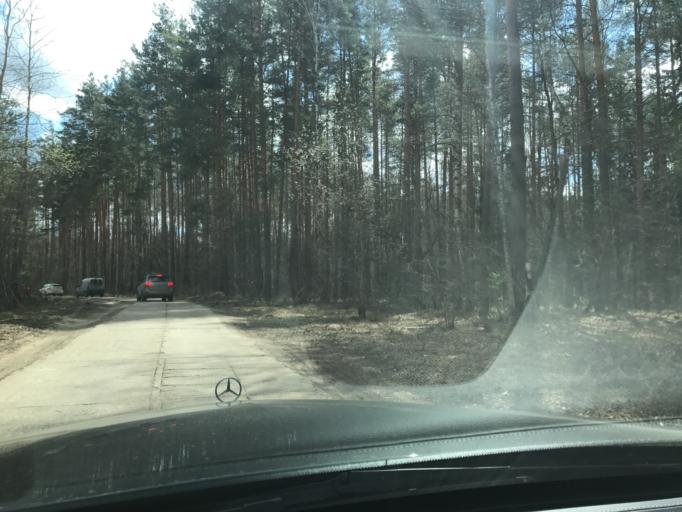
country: RU
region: Moskovskaya
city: Vereya
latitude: 55.8392
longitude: 39.1178
